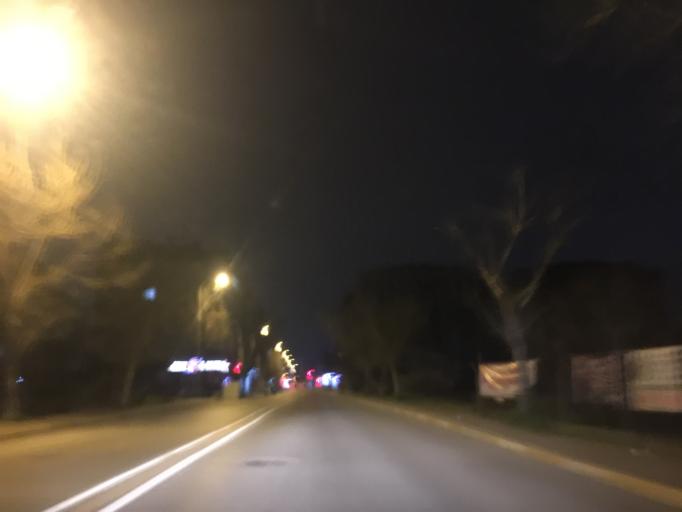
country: TR
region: Istanbul
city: Icmeler
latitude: 40.8232
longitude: 29.3099
